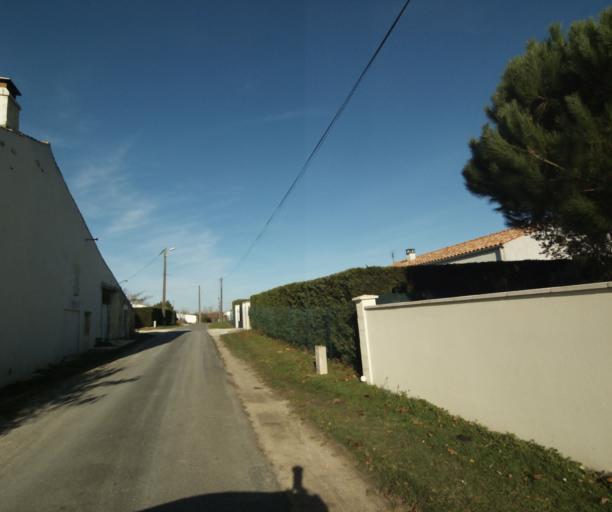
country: FR
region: Poitou-Charentes
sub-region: Departement de la Charente-Maritime
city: Ecoyeux
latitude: 45.7814
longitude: -0.5044
